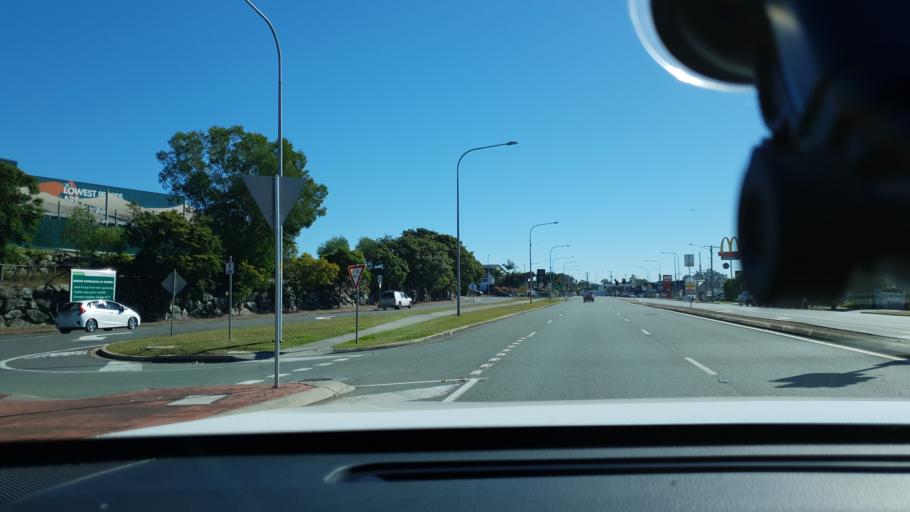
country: AU
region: Queensland
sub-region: Logan
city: Springwood
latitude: -27.6111
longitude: 153.1124
